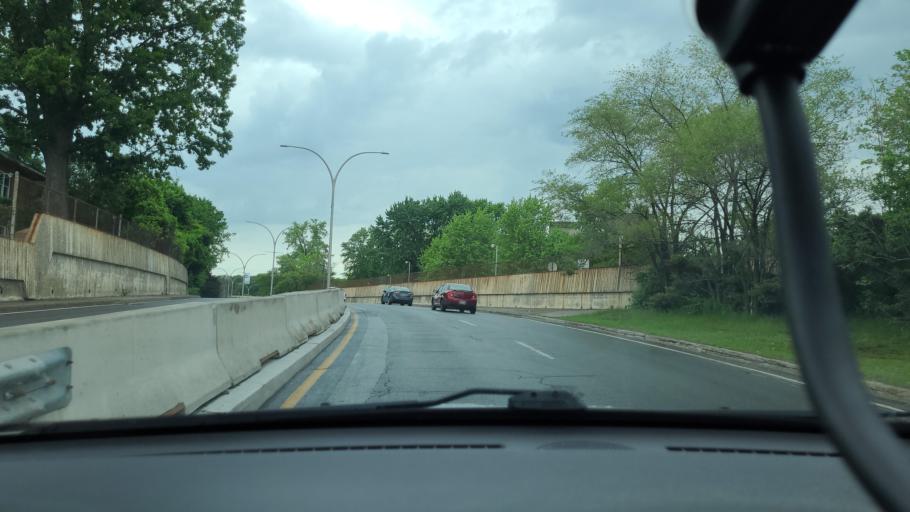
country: CA
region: Quebec
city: Sainte-Anne-de-Bellevue
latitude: 45.4088
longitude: -73.9508
